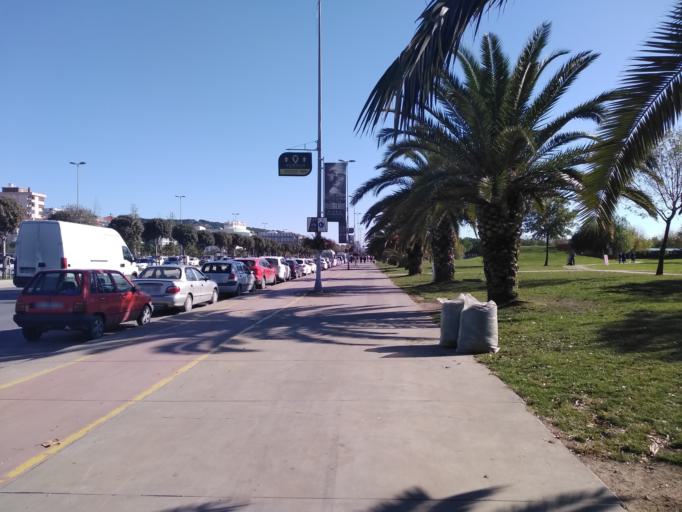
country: TR
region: Istanbul
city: Maltepe
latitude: 40.9174
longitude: 29.1303
